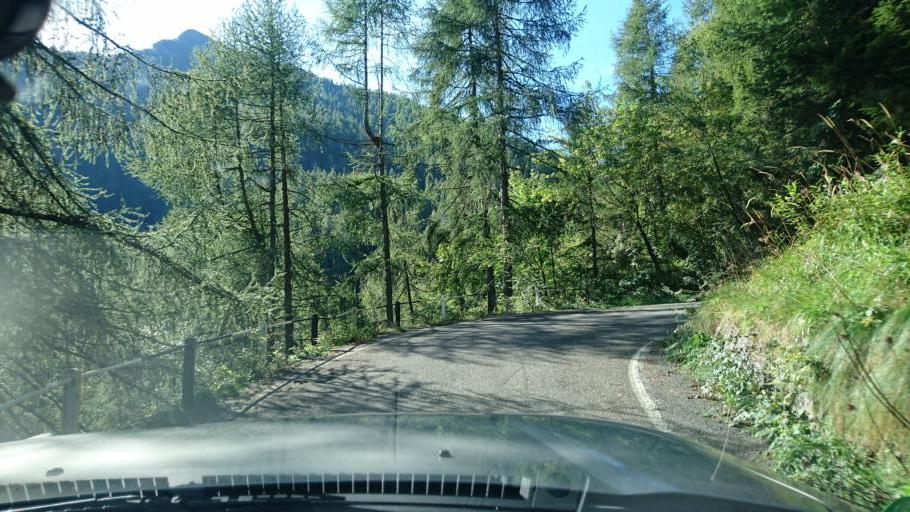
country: IT
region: Lombardy
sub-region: Provincia di Brescia
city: Lozio
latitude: 46.0448
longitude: 10.2229
